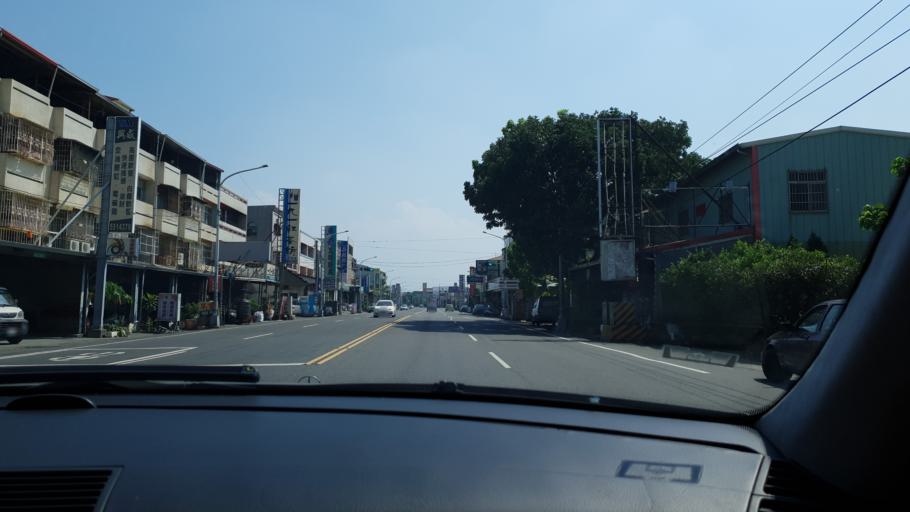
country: TW
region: Taiwan
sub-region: Yunlin
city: Douliu
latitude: 23.7224
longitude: 120.5256
